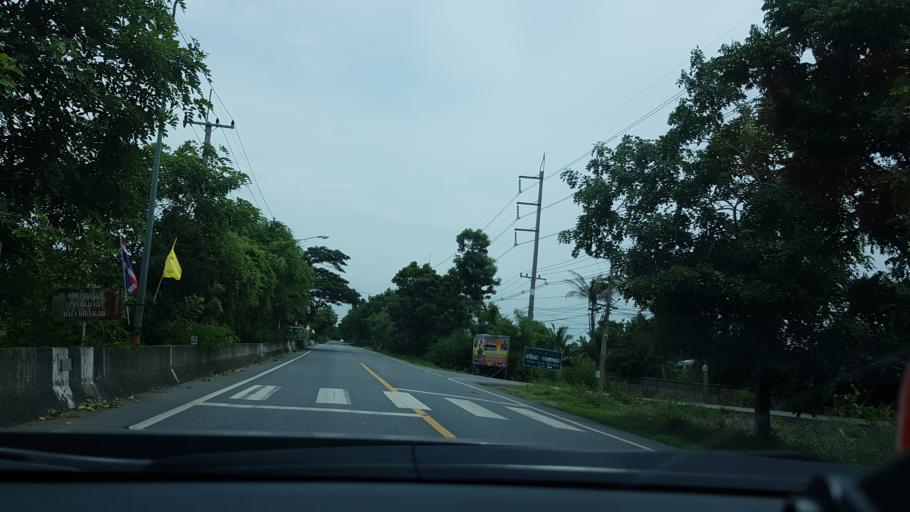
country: TH
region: Pathum Thani
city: Sam Khok
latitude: 14.1341
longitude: 100.5325
